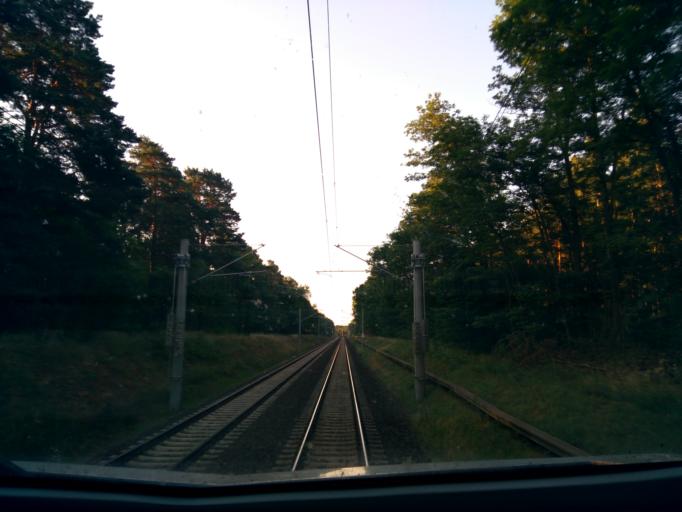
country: DE
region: Brandenburg
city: Gross Koris
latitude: 52.1739
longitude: 13.6425
